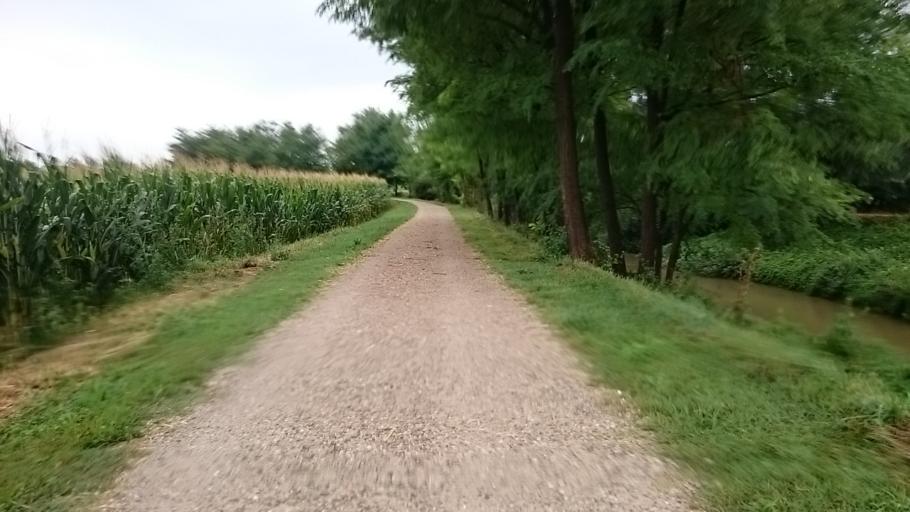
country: IT
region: Veneto
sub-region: Provincia di Treviso
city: Villa d'Asolo
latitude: 45.7902
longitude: 11.8939
